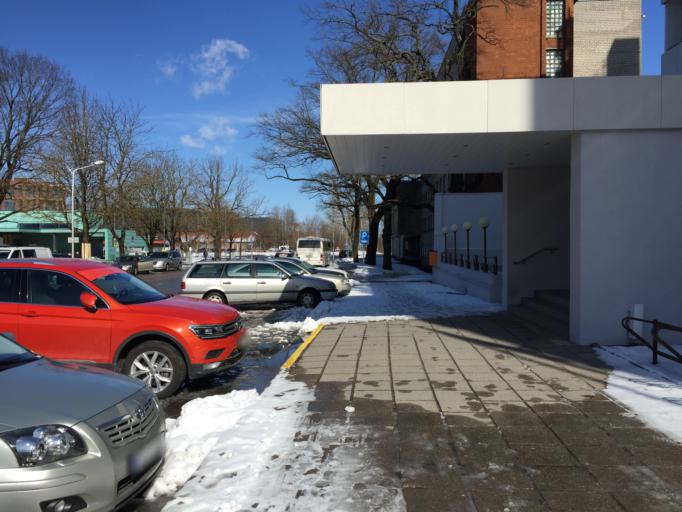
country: EE
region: Paernumaa
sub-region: Paernu linn
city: Parnu
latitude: 58.3851
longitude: 24.5065
